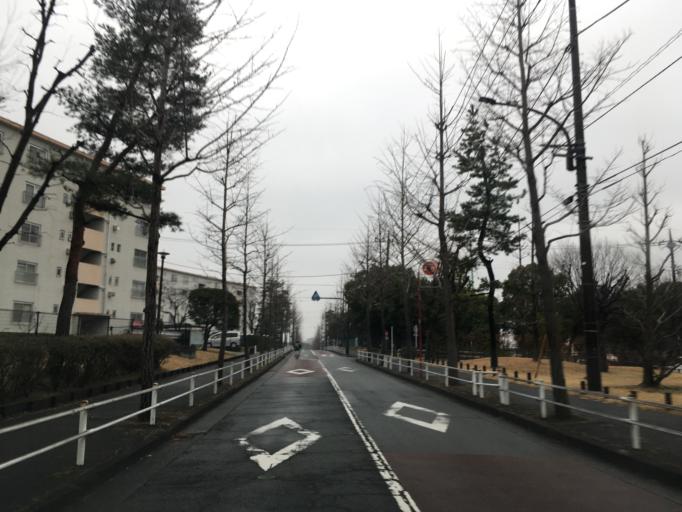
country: JP
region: Tokyo
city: Hino
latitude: 35.6192
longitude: 139.4515
